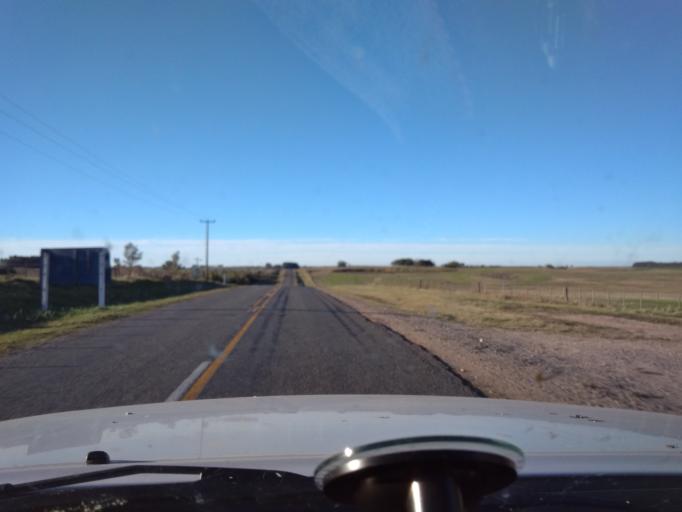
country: UY
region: Canelones
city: San Ramon
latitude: -34.0847
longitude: -55.9207
